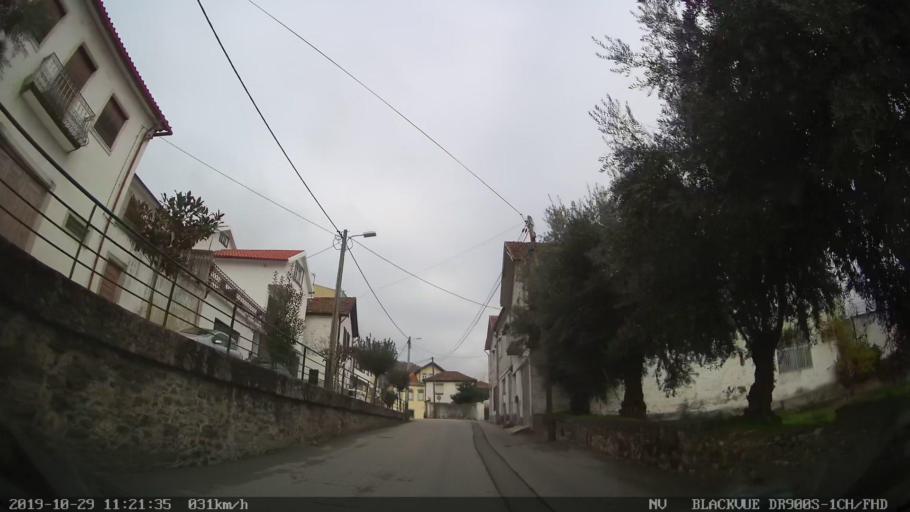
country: PT
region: Vila Real
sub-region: Peso da Regua
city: Godim
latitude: 41.1642
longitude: -7.8043
